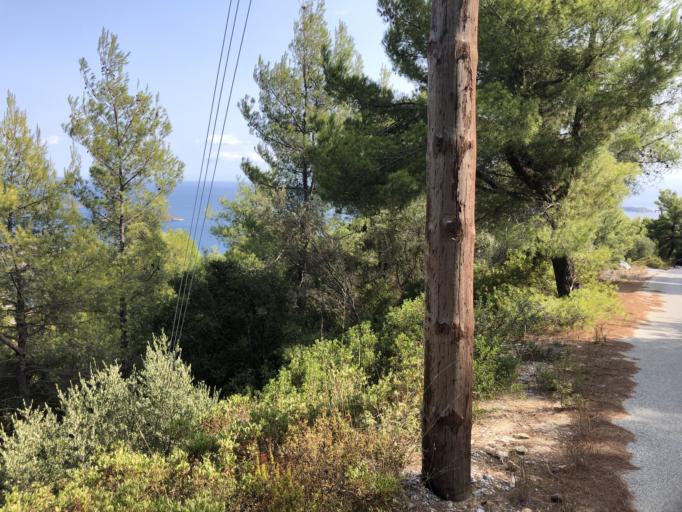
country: GR
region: Thessaly
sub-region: Nomos Magnisias
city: Skiathos
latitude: 39.1665
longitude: 23.4684
